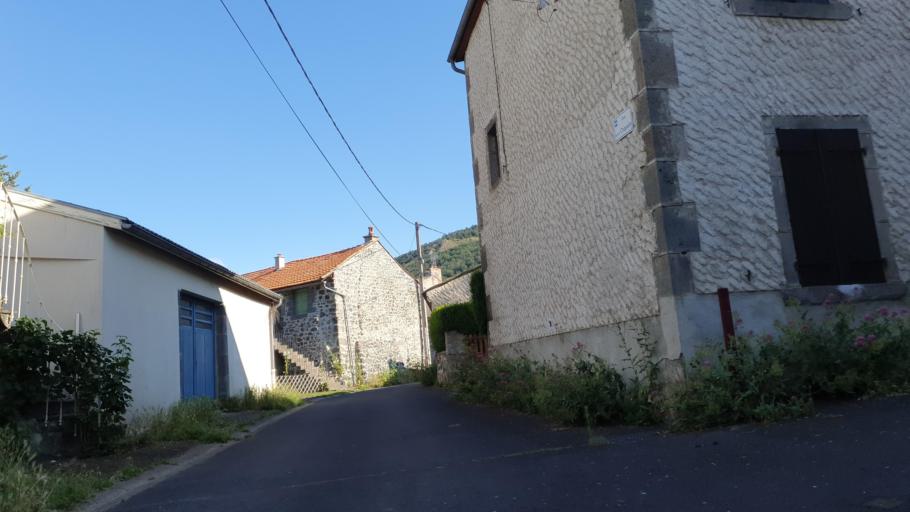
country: FR
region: Auvergne
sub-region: Departement du Puy-de-Dome
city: Aydat
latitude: 45.5731
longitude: 3.0147
